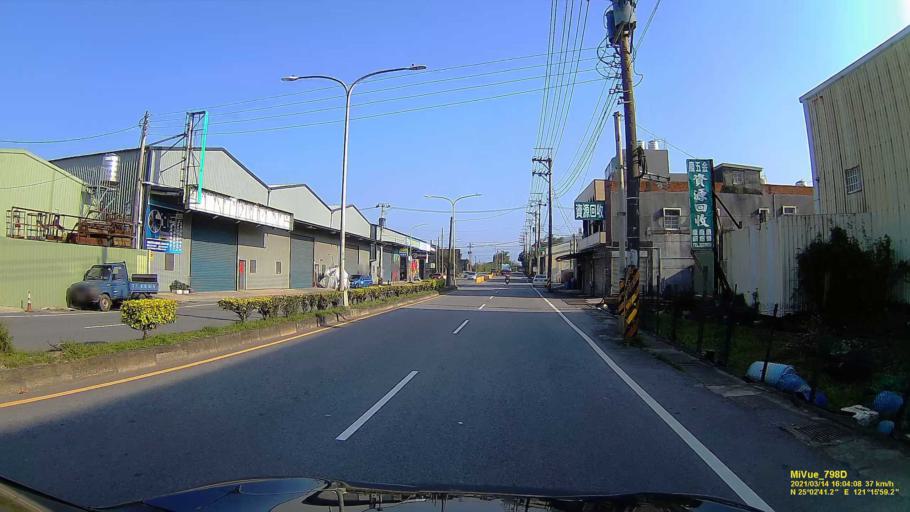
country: TW
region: Taiwan
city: Taoyuan City
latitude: 25.0446
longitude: 121.2665
